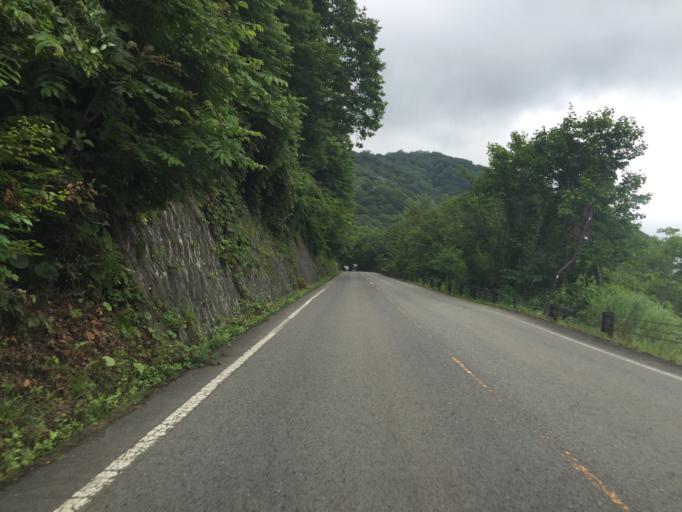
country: JP
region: Fukushima
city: Inawashiro
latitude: 37.7015
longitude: 140.0604
